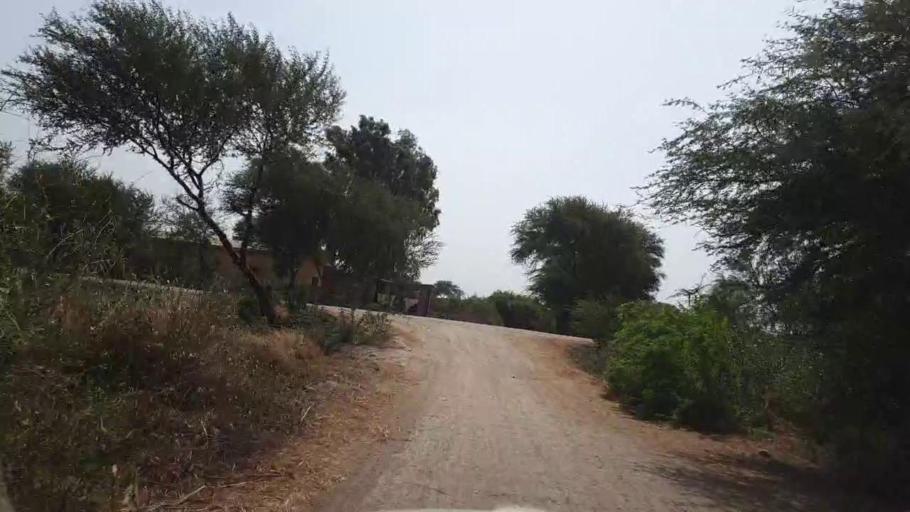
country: PK
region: Sindh
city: Matli
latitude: 25.0364
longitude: 68.7036
